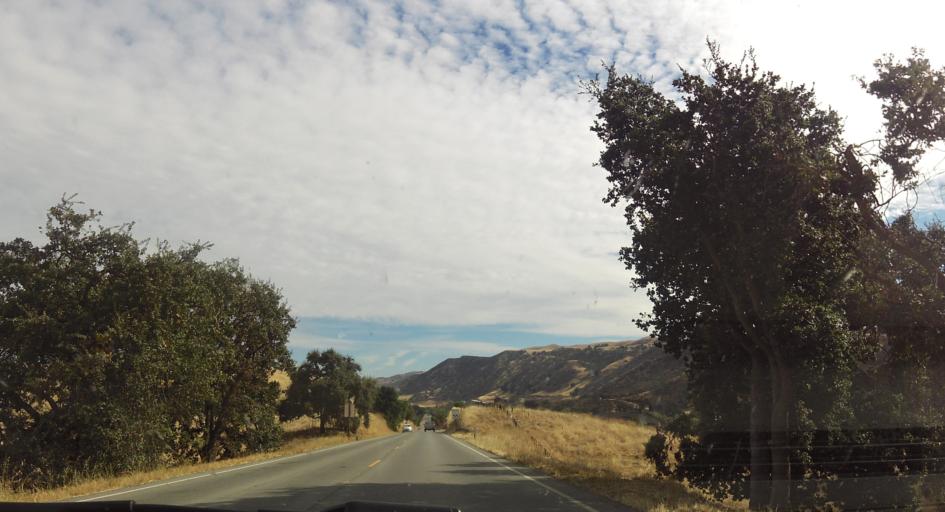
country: US
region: California
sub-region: San Benito County
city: Ridgemark
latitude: 36.7840
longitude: -121.3144
